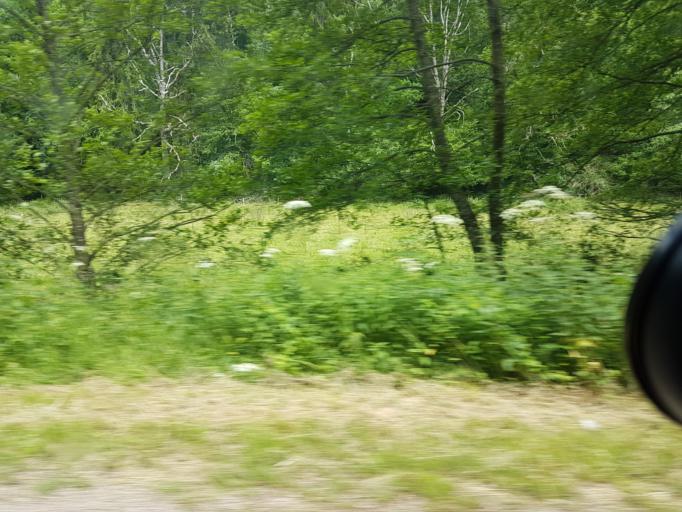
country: FR
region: Bourgogne
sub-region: Departement de la Cote-d'Or
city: Saulieu
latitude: 47.1669
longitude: 4.1784
